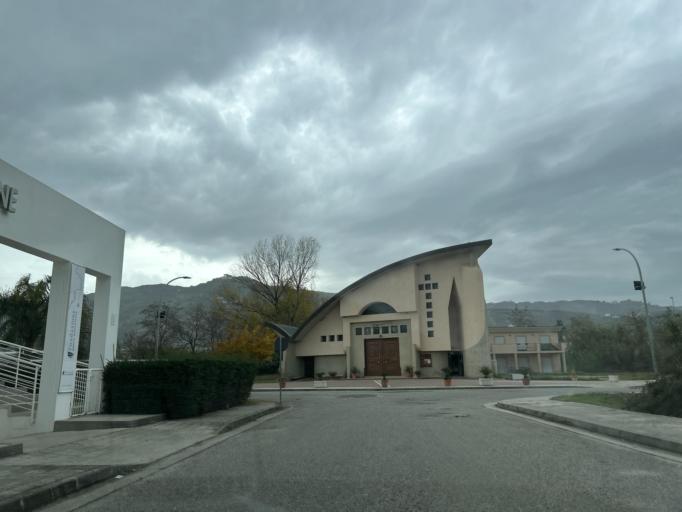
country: IT
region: Calabria
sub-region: Provincia di Catanzaro
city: Montepaone Lido
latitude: 38.7273
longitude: 16.5384
